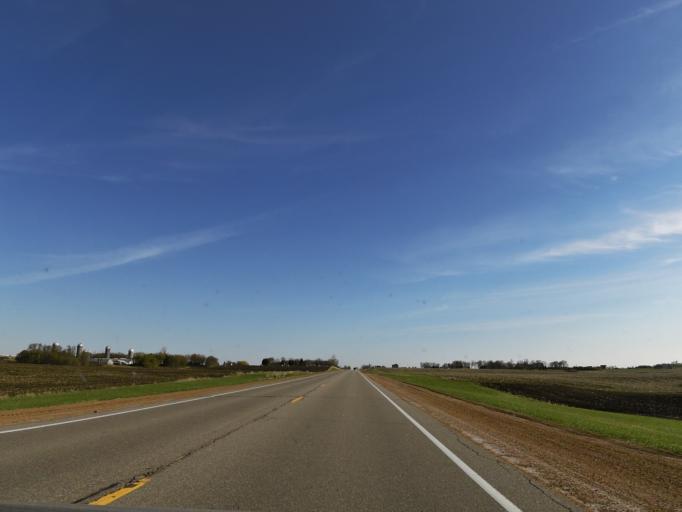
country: US
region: Minnesota
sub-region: Le Sueur County
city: New Prague
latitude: 44.6101
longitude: -93.5016
